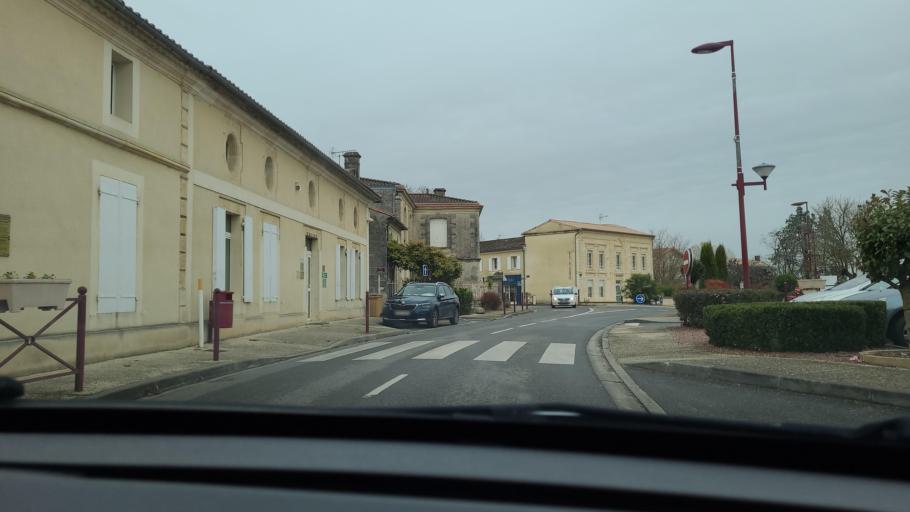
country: FR
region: Aquitaine
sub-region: Departement de la Gironde
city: Pugnac
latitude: 45.0821
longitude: -0.4966
